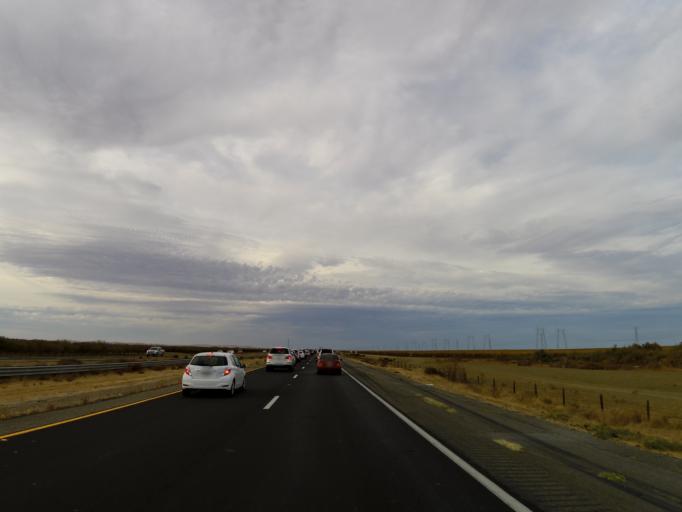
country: US
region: California
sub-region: Kings County
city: Kettleman City
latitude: 35.8602
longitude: -119.8379
